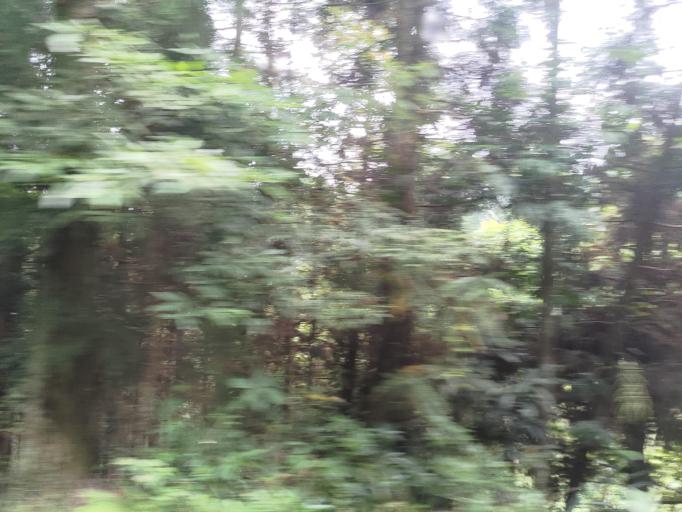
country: TW
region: Taiwan
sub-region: Hsinchu
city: Hsinchu
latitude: 24.6222
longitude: 121.0905
